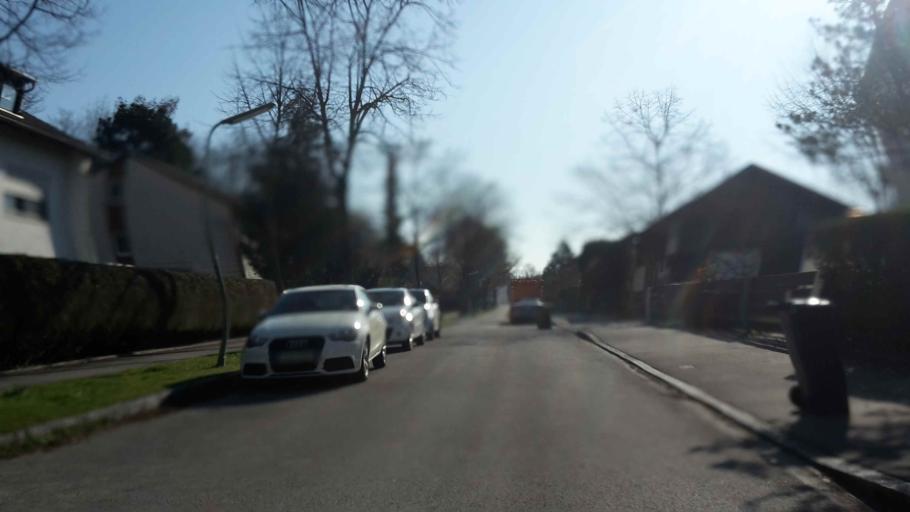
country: DE
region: Bavaria
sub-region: Upper Bavaria
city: Unterfoehring
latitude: 48.1998
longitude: 11.6218
